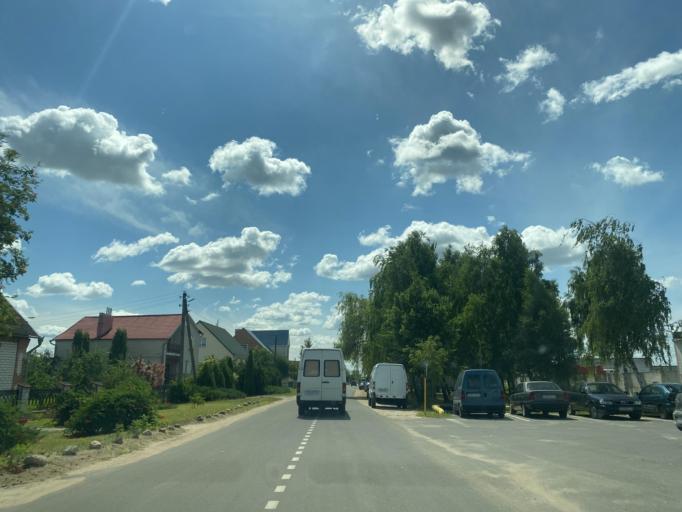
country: BY
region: Brest
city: Ivanava
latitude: 52.1459
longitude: 25.5465
